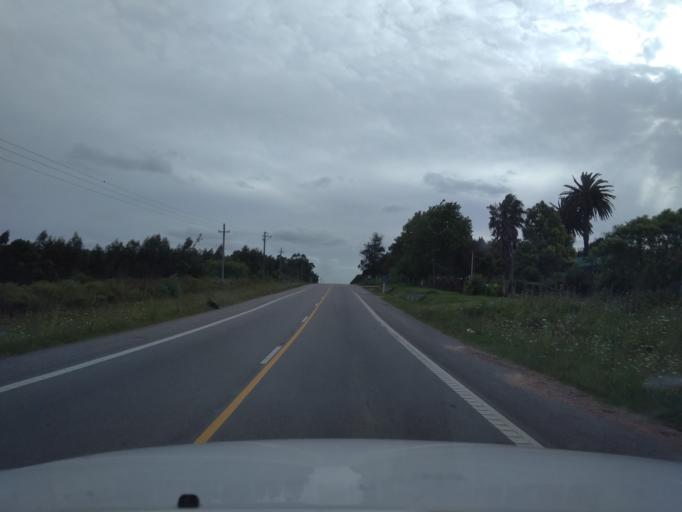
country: UY
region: Canelones
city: Joaquin Suarez
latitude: -34.6896
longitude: -56.0271
